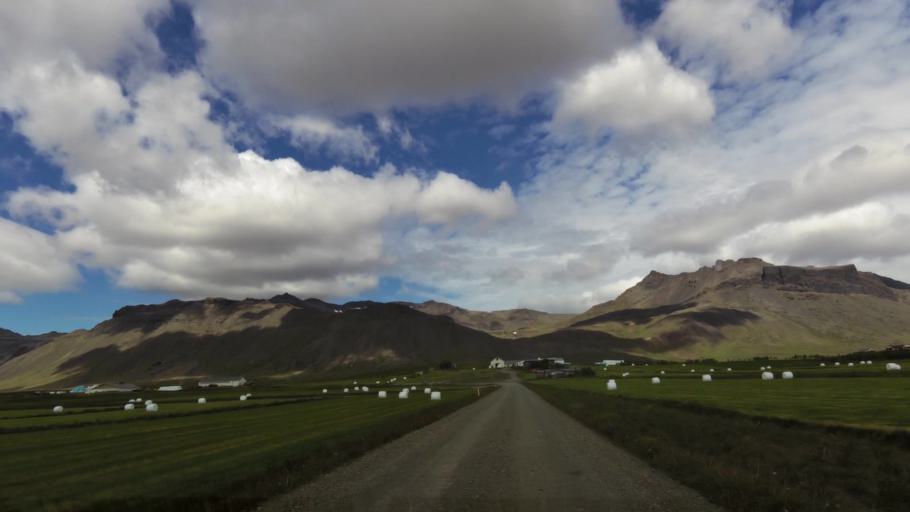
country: IS
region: West
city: Stykkisholmur
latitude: 64.8342
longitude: -22.9755
